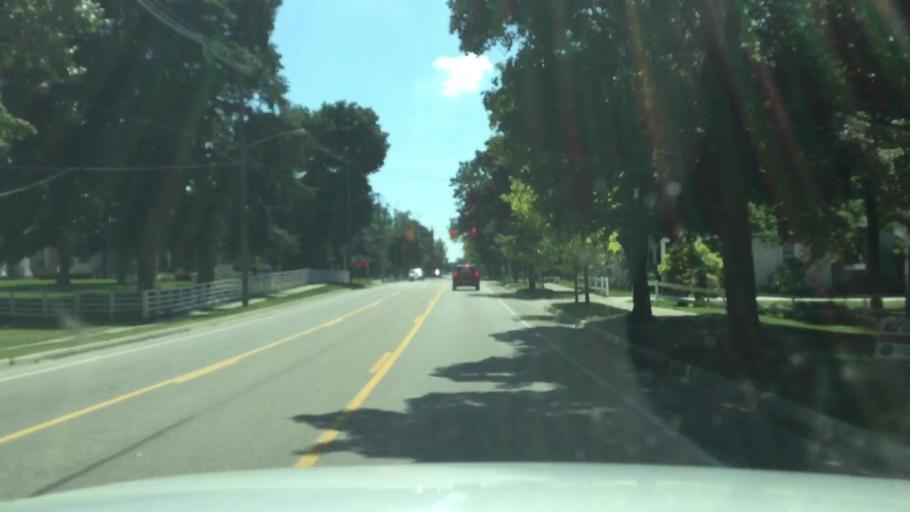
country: US
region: Michigan
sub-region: Lenawee County
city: Clinton
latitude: 42.0711
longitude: -83.9712
